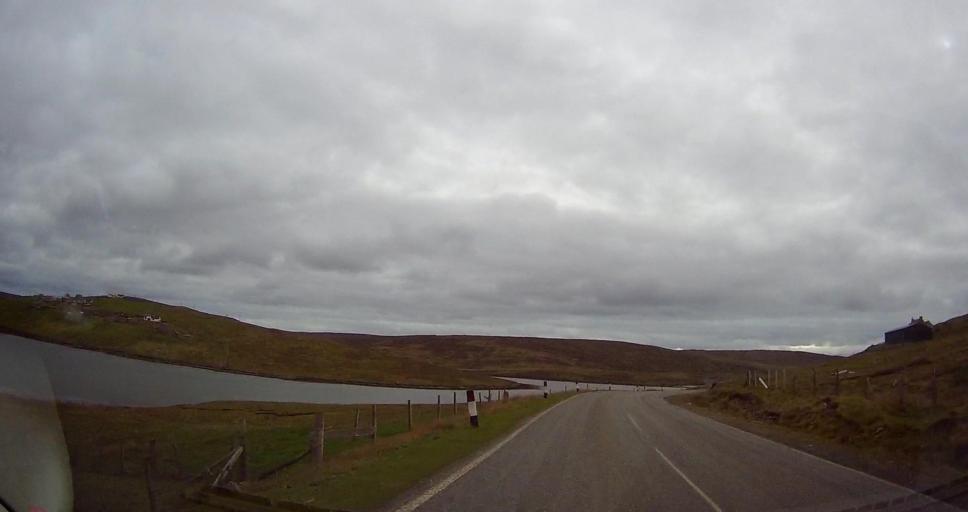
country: GB
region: Scotland
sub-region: Shetland Islands
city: Shetland
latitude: 60.6096
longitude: -1.0754
